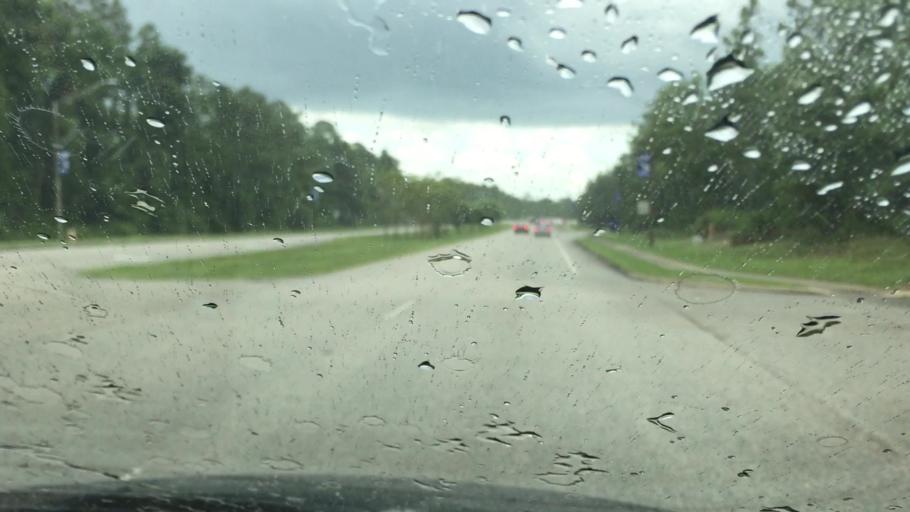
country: US
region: Florida
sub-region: Duval County
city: Jacksonville Beach
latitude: 30.2577
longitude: -81.4994
